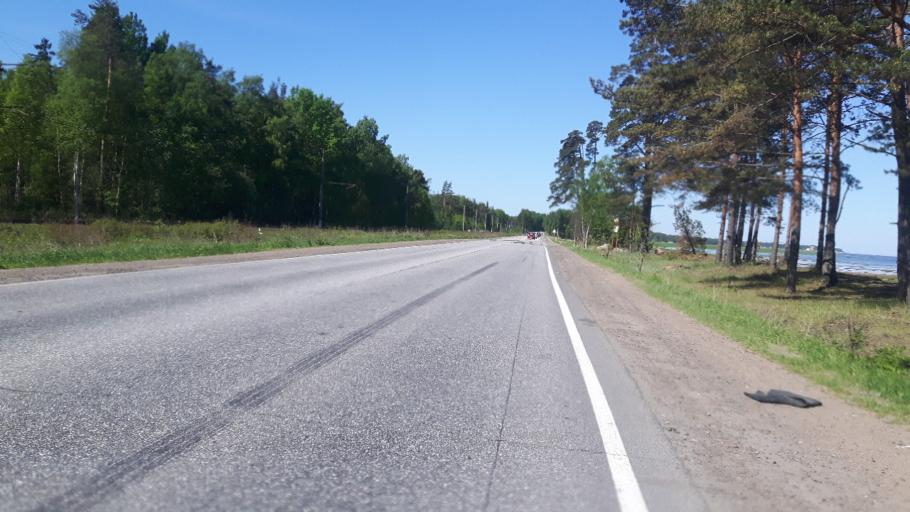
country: RU
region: Leningrad
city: Lebyazh'ye
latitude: 59.9570
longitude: 29.4868
